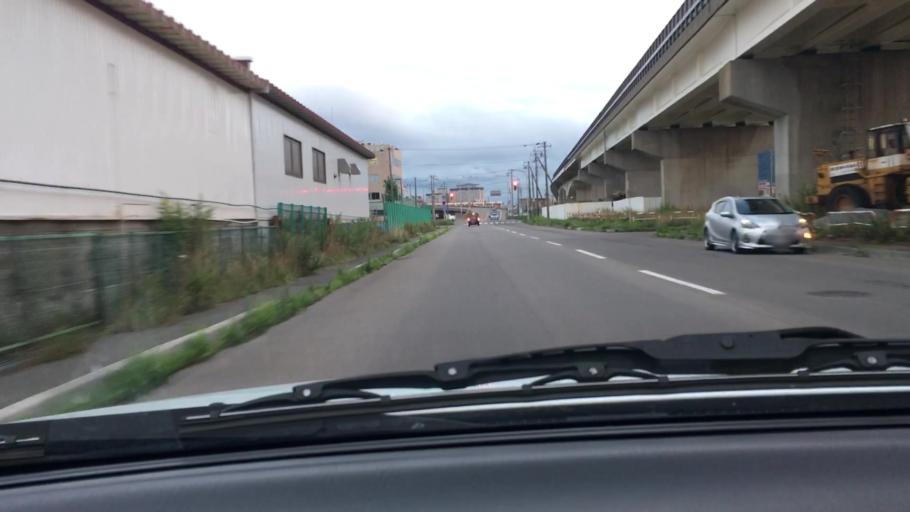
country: JP
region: Hokkaido
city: Hakodate
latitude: 41.7843
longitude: 140.7271
